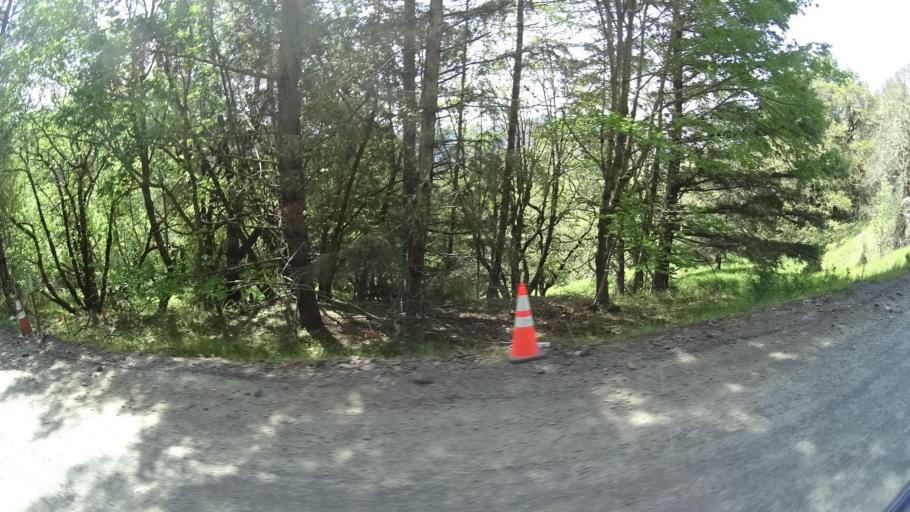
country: US
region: California
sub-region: Humboldt County
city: Redway
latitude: 40.4016
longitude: -123.7465
